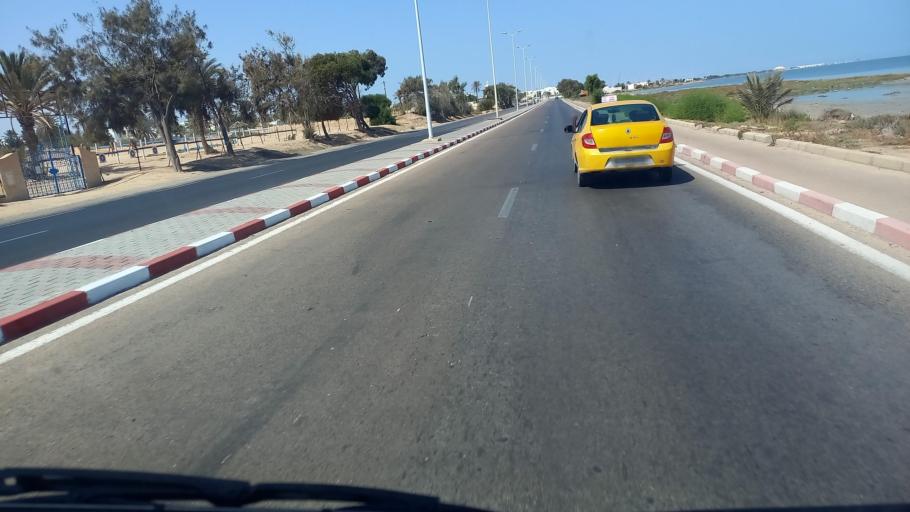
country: TN
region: Madanin
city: Houmt Souk
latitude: 33.8734
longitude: 10.9153
